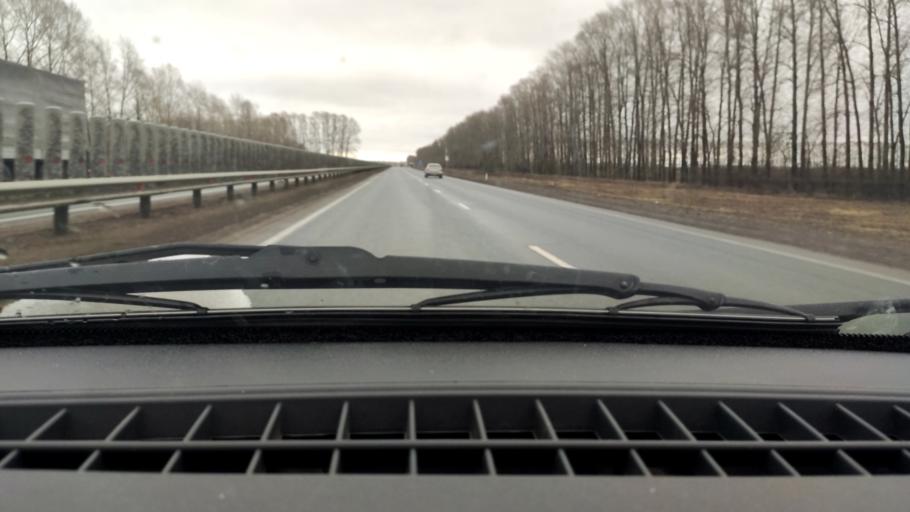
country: RU
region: Bashkortostan
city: Asanovo
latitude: 55.0198
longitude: 55.4744
